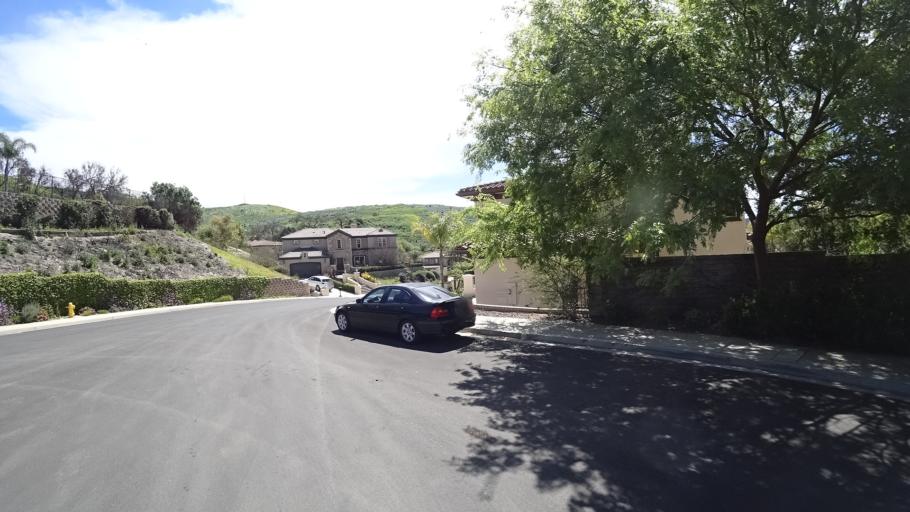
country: US
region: California
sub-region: Ventura County
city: Thousand Oaks
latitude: 34.1816
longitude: -118.8388
